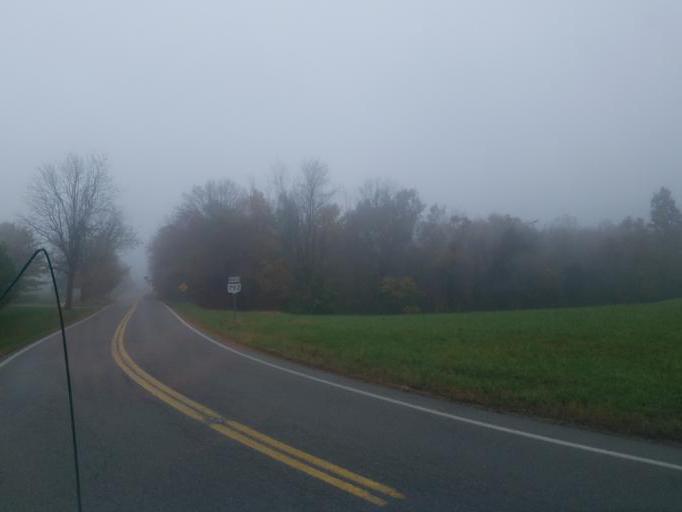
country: US
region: Ohio
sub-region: Morgan County
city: McConnelsville
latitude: 39.5236
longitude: -81.7935
